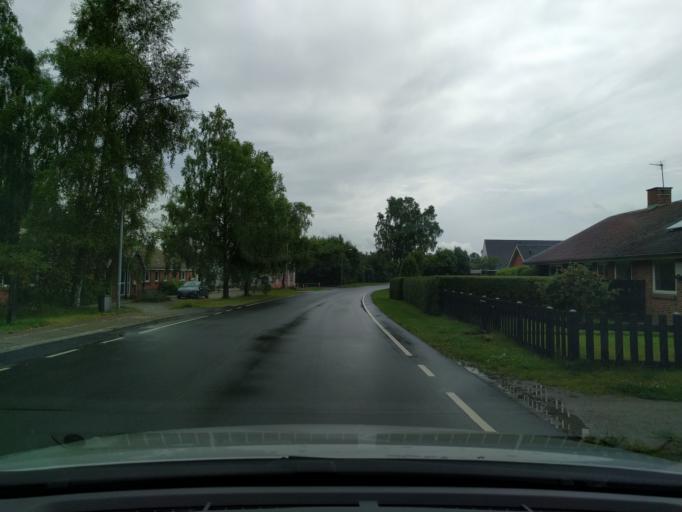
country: DK
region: Central Jutland
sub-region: Skanderborg Kommune
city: Ry
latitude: 56.0878
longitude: 9.7784
